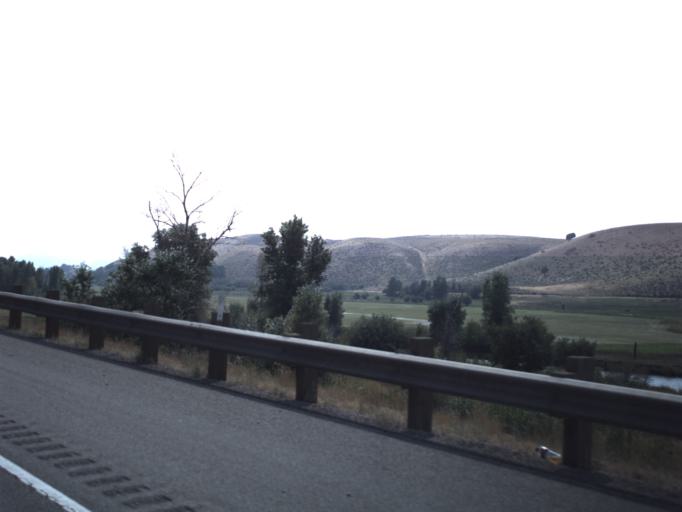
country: US
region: Utah
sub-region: Summit County
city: Coalville
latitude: 40.8491
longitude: -111.3896
